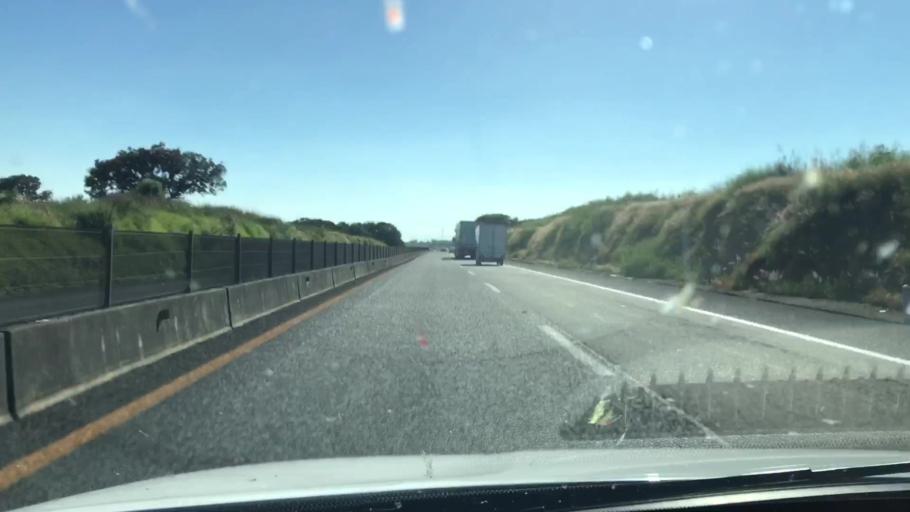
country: MX
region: Jalisco
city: Tepatitlan de Morelos
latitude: 20.8575
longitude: -102.7679
